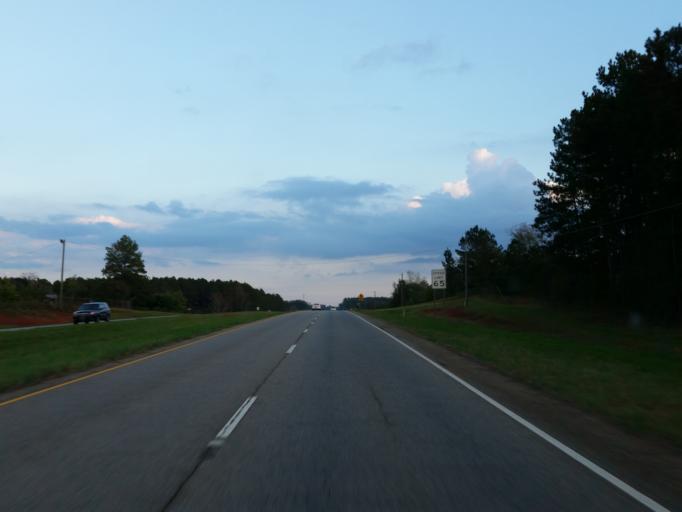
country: US
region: Georgia
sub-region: Pulaski County
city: Hawkinsville
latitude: 32.3587
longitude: -83.5951
